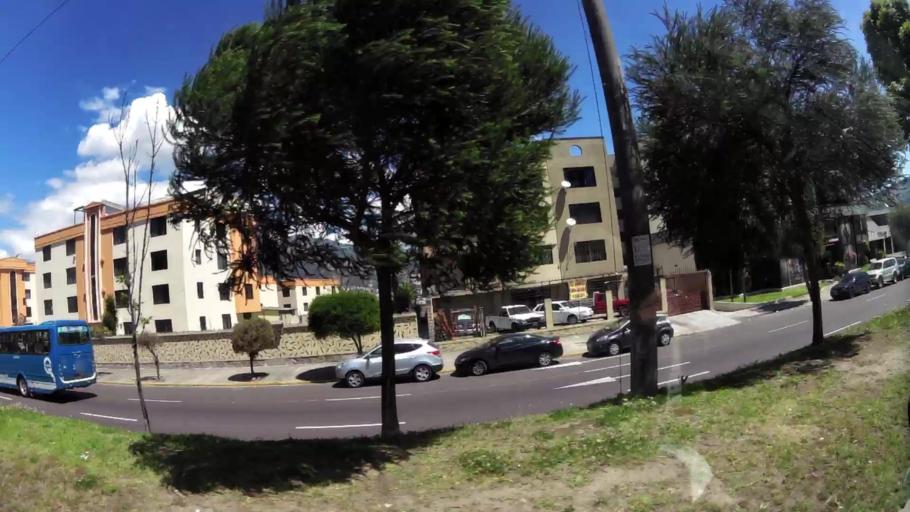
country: EC
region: Pichincha
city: Quito
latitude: -0.1037
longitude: -78.4832
